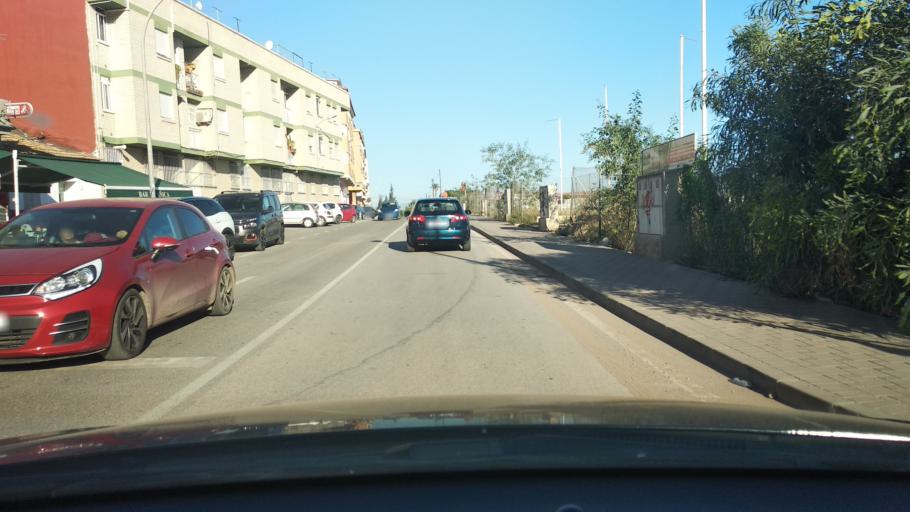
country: ES
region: Murcia
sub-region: Murcia
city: Murcia
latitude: 37.9422
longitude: -1.1169
